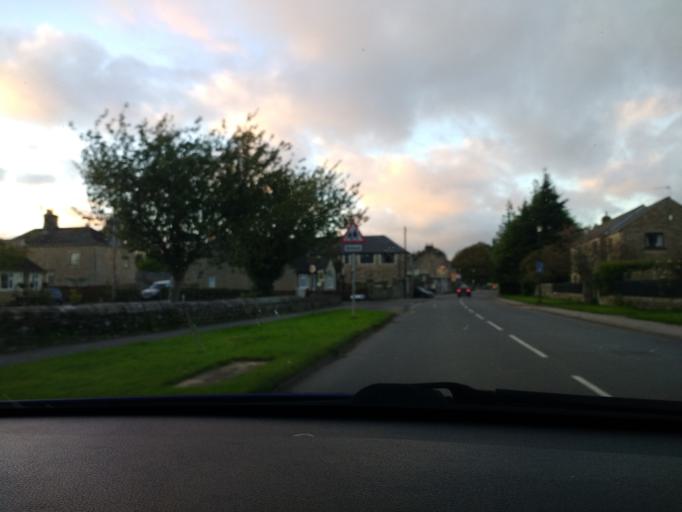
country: GB
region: England
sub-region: Lancashire
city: Caton
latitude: 54.1153
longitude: -2.6374
